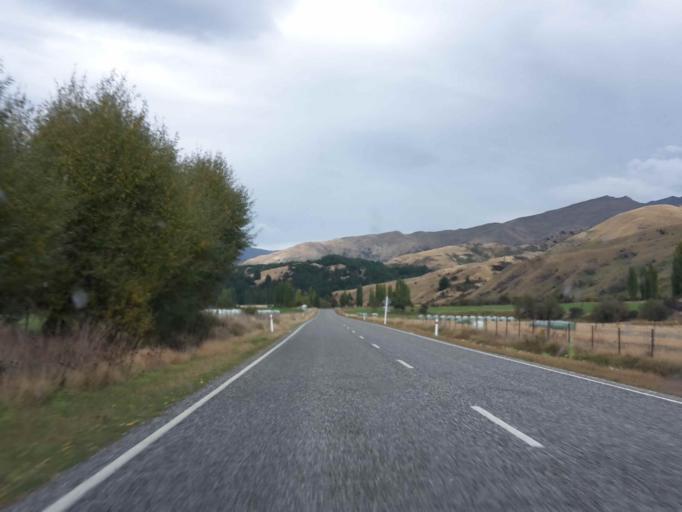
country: NZ
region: Otago
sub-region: Queenstown-Lakes District
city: Wanaka
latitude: -44.7528
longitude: 169.1136
